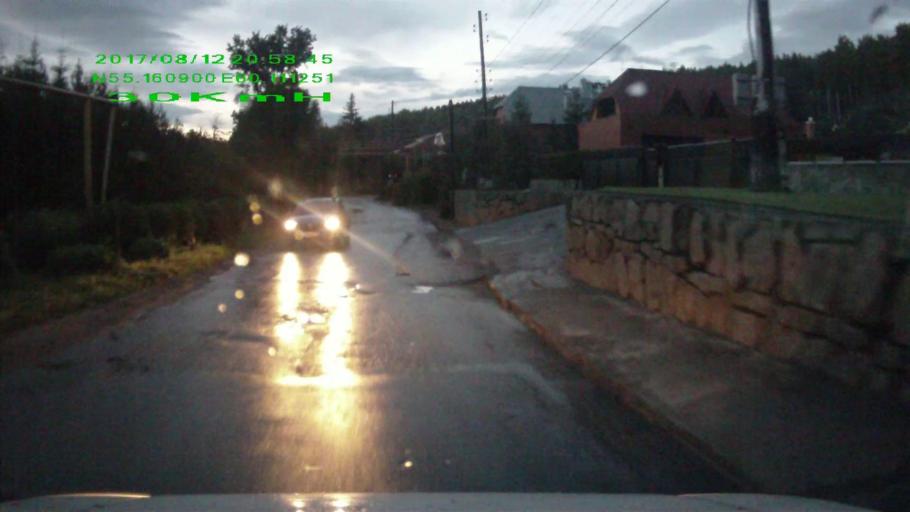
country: RU
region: Chelyabinsk
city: Turgoyak
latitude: 55.1609
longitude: 60.1113
